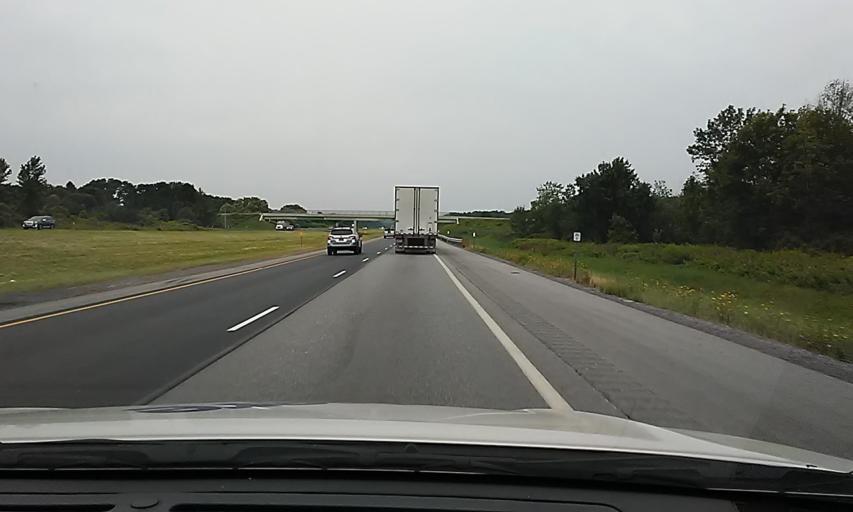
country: US
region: New York
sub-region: Genesee County
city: Le Roy
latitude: 43.0241
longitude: -78.0623
